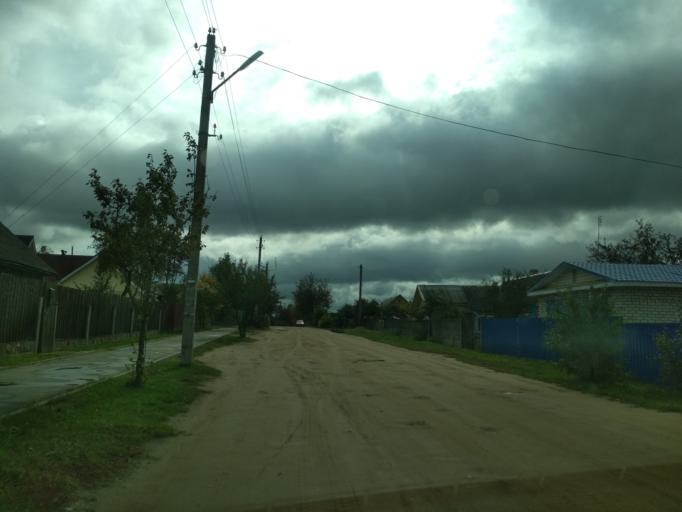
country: BY
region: Minsk
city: Mar''ina Horka
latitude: 53.5089
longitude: 28.1468
